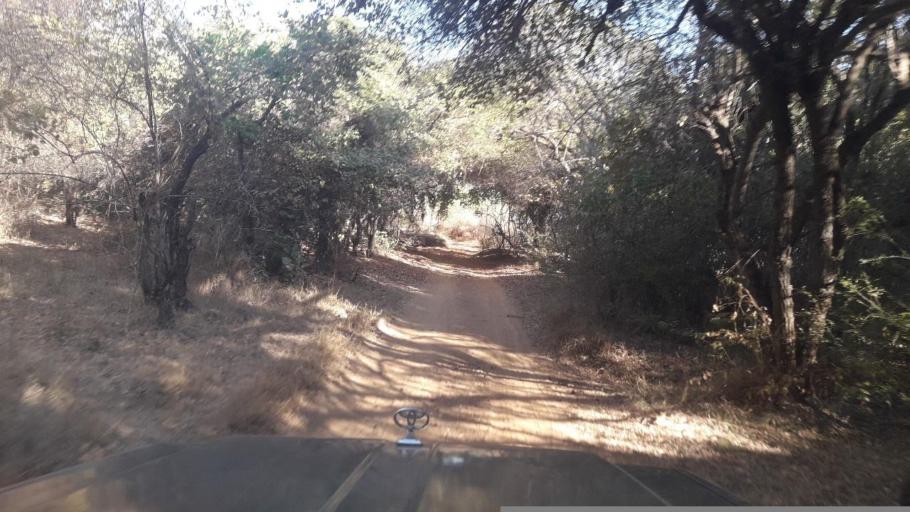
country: MG
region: Boeny
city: Sitampiky
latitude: -16.4033
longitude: 45.5980
